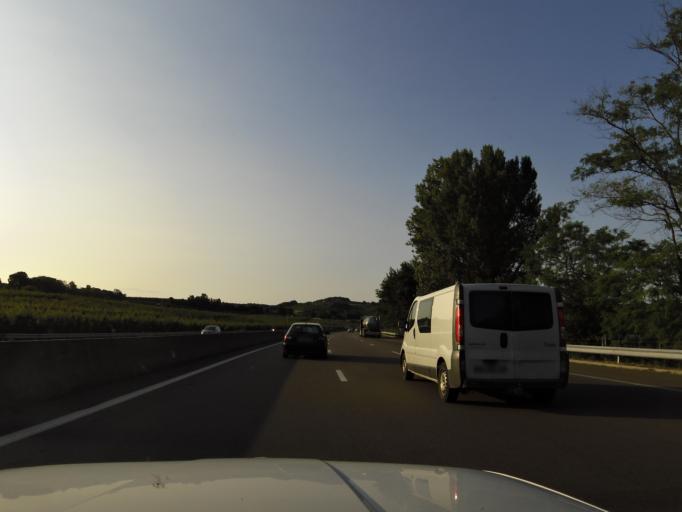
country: FR
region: Rhone-Alpes
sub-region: Departement de la Drome
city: Mercurol
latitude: 45.0964
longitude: 4.8783
